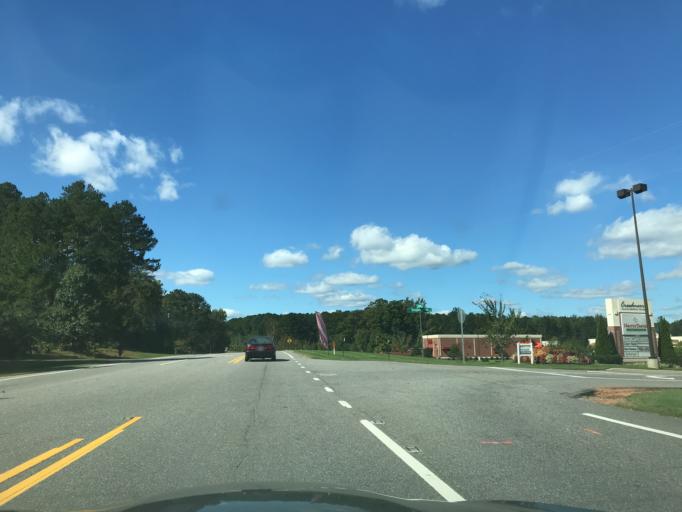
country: US
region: North Carolina
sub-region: Granville County
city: Creedmoor
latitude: 35.9885
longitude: -78.6915
